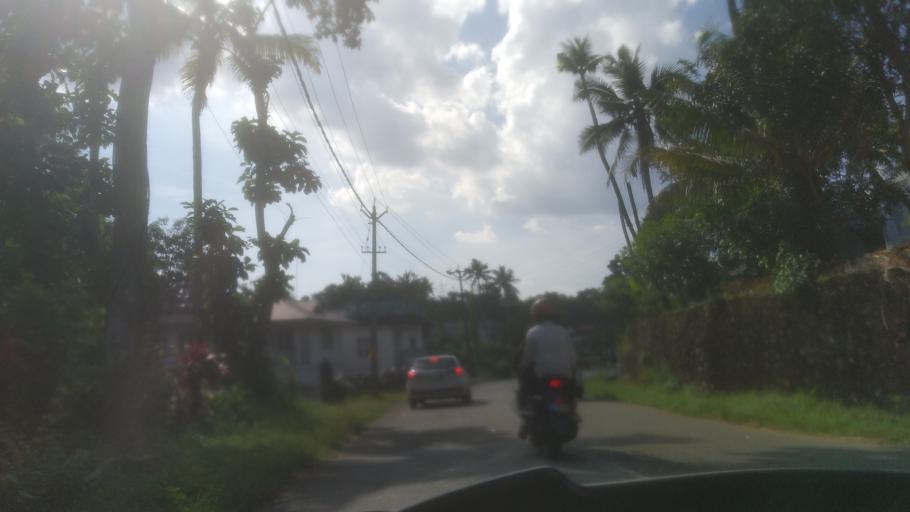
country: IN
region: Kerala
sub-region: Ernakulam
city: Muvattupula
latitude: 9.9975
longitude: 76.6156
